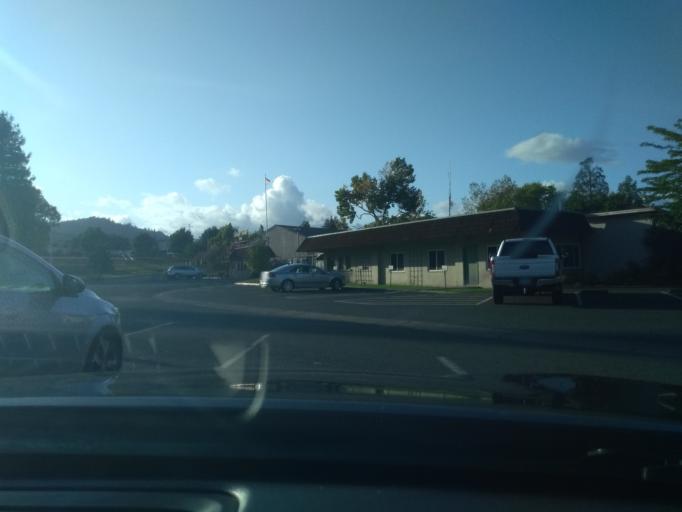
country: US
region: California
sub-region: Mendocino County
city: Ukiah
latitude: 39.1626
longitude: -123.2077
